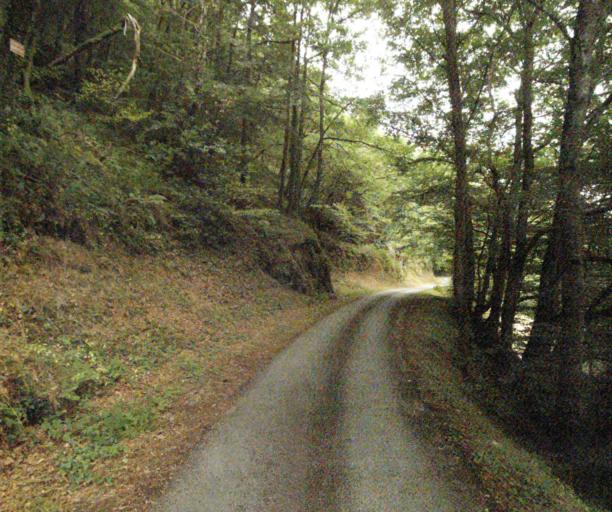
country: FR
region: Midi-Pyrenees
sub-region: Departement du Tarn
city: Soreze
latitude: 43.4196
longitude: 2.0848
